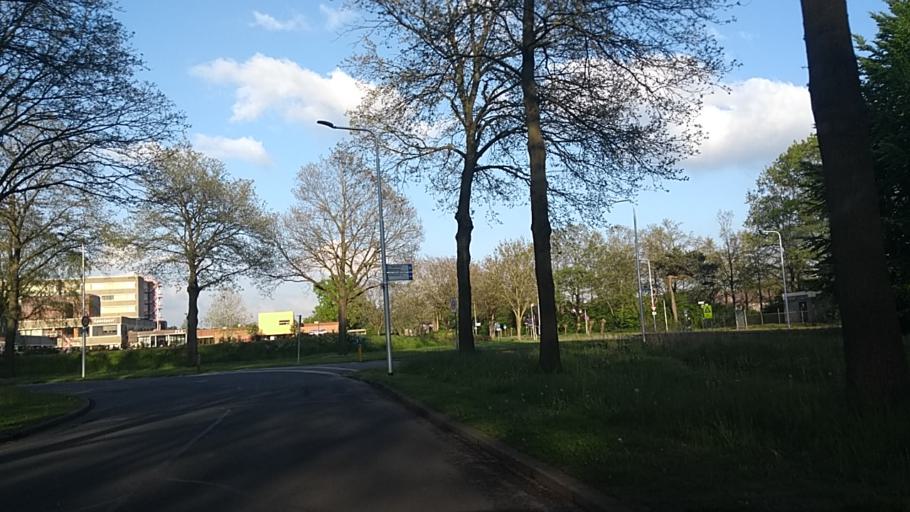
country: NL
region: Overijssel
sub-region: Gemeente Almelo
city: Almelo
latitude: 52.3359
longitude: 6.6371
